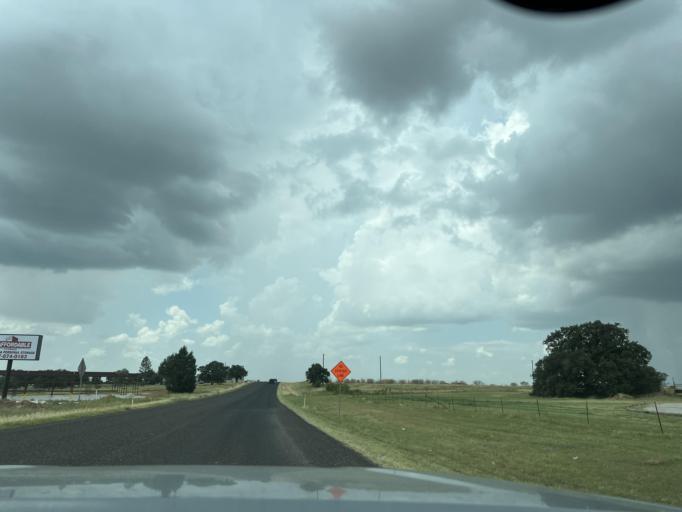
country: US
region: Texas
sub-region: Wise County
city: Decatur
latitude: 33.1779
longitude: -97.6203
